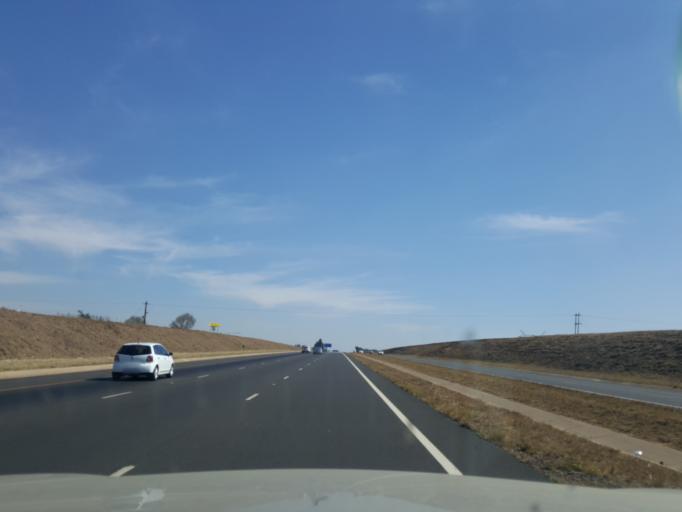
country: ZA
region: Mpumalanga
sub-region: Nkangala District Municipality
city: Middelburg
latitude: -25.8314
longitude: 29.4838
